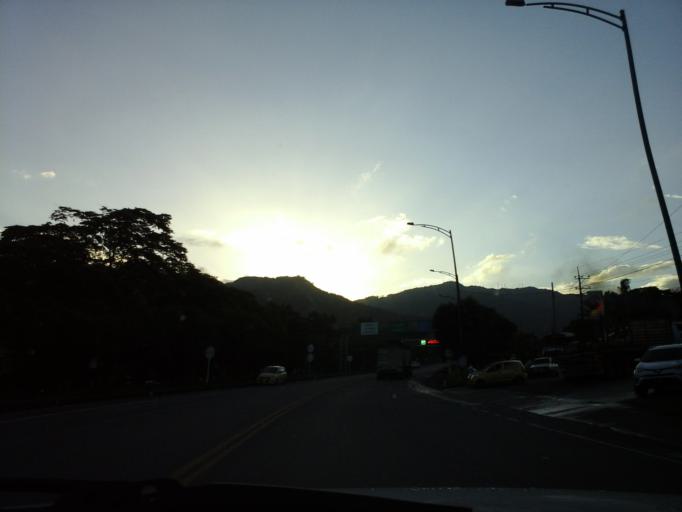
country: CO
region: Meta
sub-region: Villavicencio
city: Villavicencio
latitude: 4.1226
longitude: -73.6462
